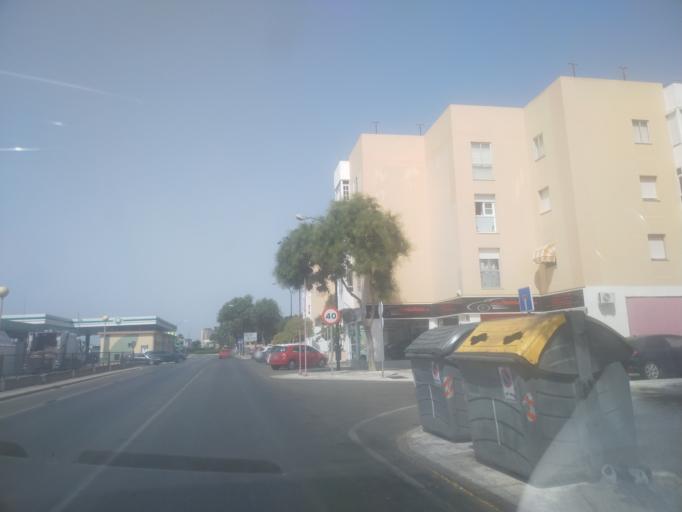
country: ES
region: Andalusia
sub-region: Provincia de Cadiz
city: San Fernando
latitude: 36.4710
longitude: -6.2037
